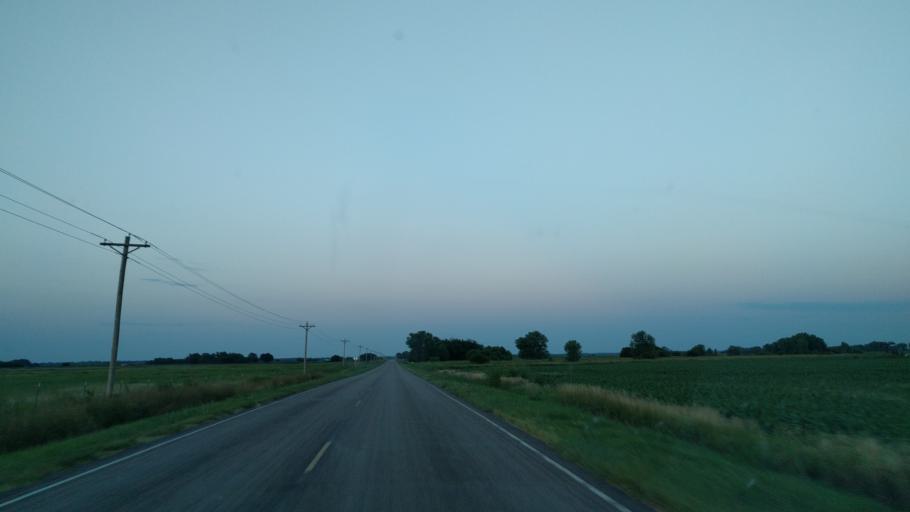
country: US
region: Kansas
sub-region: Reno County
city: Nickerson
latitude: 38.2176
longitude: -98.1245
